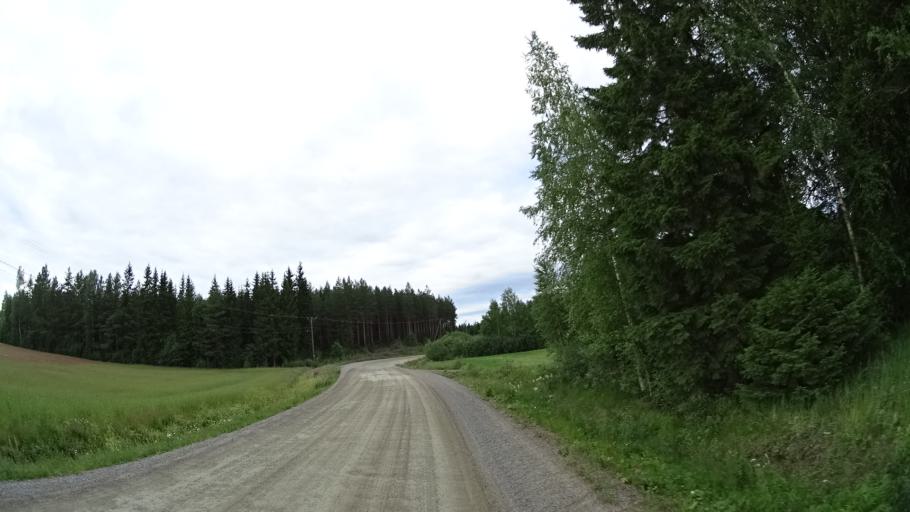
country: FI
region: Satakunta
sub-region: Pohjois-Satakunta
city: Jaemijaervi
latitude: 61.7729
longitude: 22.8593
